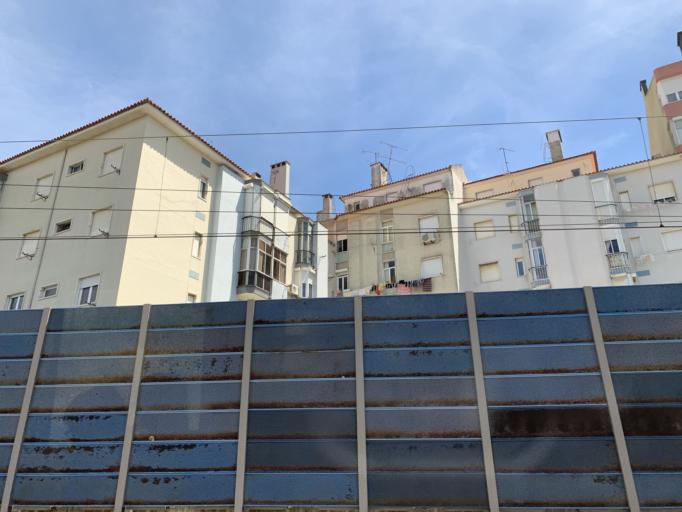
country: PT
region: Lisbon
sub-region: Amadora
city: Amadora
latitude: 38.7559
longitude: -9.2284
